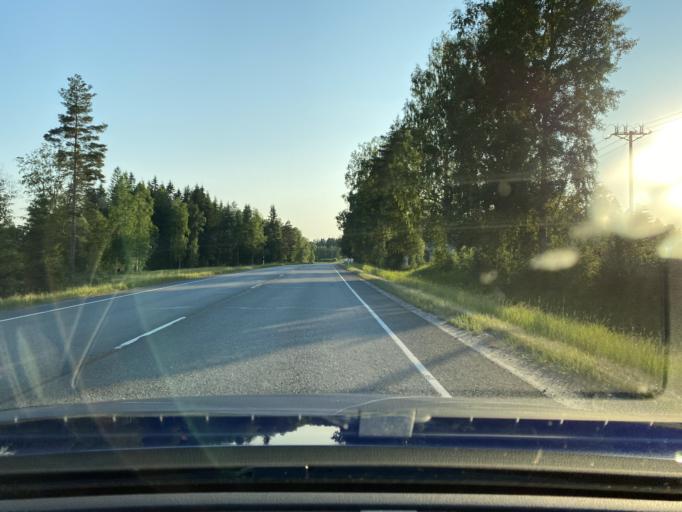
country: FI
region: Haeme
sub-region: Forssa
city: Tammela
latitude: 60.8255
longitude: 23.9793
